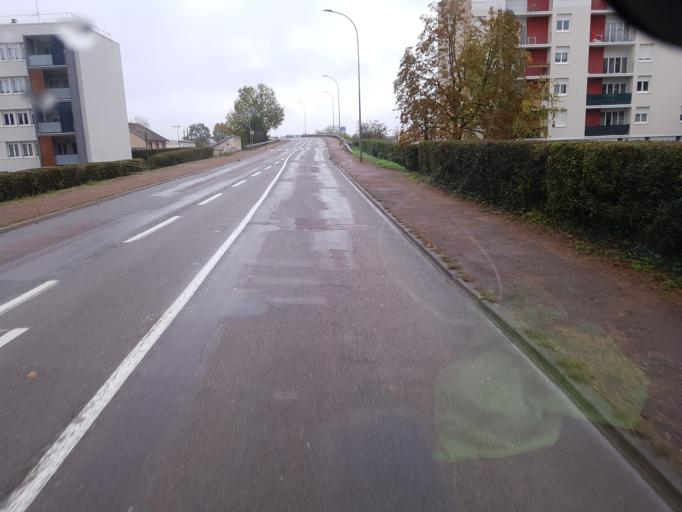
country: FR
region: Bourgogne
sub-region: Departement de la Cote-d'Or
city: Genlis
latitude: 47.2420
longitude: 5.2246
